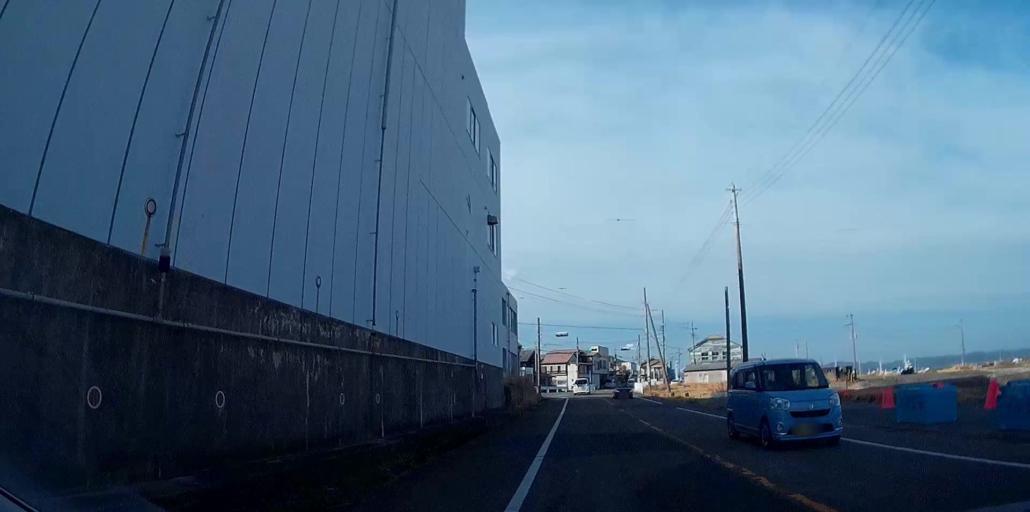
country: JP
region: Chiba
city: Tateyama
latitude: 34.9588
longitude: 139.9619
